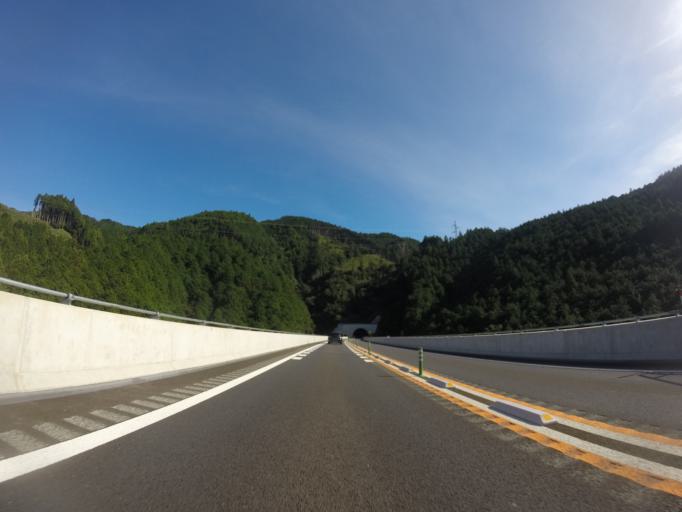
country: JP
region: Shizuoka
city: Fujinomiya
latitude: 35.2111
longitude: 138.4601
